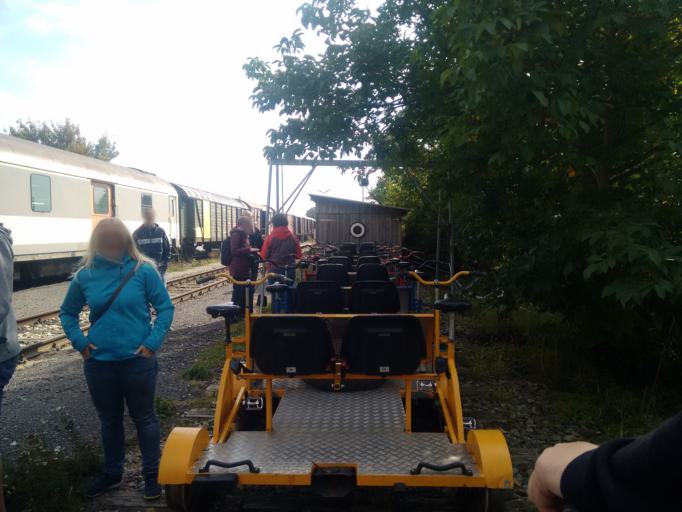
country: AT
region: Lower Austria
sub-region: Politischer Bezirk Mistelbach
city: Asparn an der Zaya
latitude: 48.5824
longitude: 16.4930
